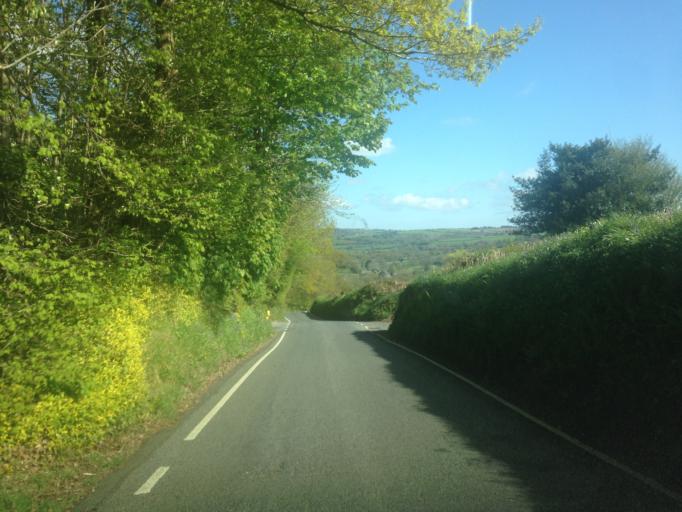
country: GB
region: Wales
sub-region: County of Ceredigion
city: Newcastle Emlyn
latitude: 52.0918
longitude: -4.4167
